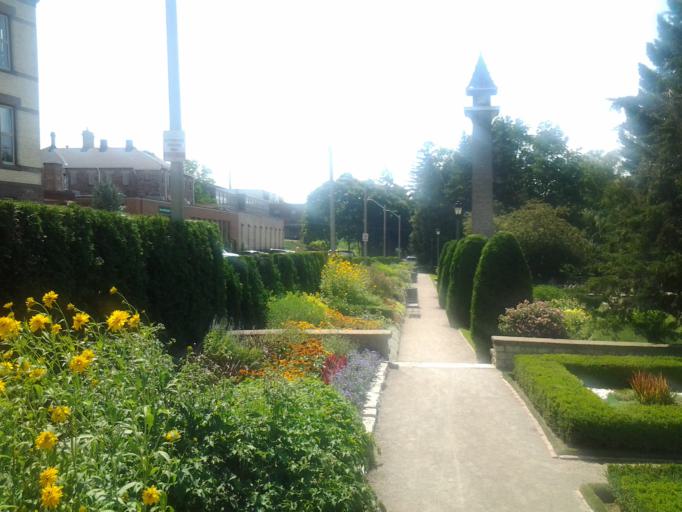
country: CA
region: Ontario
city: Stratford
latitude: 43.3719
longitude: -80.9848
